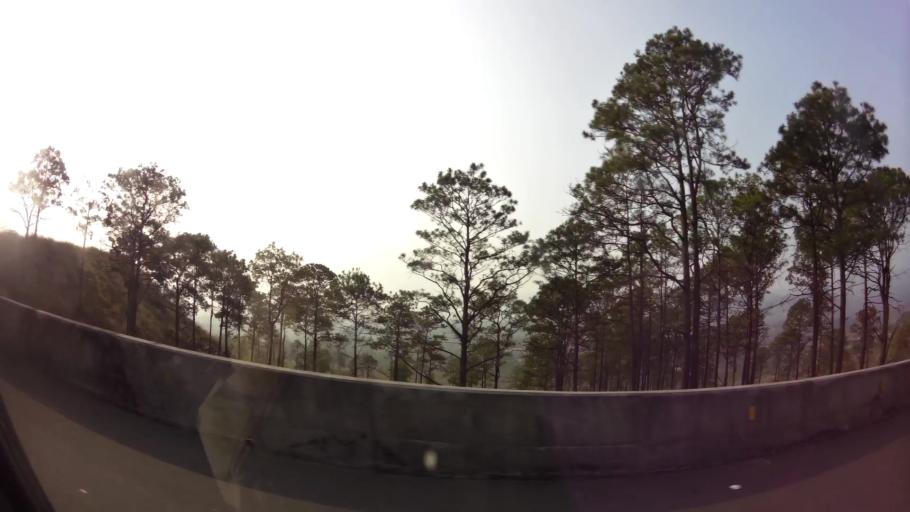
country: HN
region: Francisco Morazan
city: Zambrano
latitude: 14.2387
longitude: -87.3860
